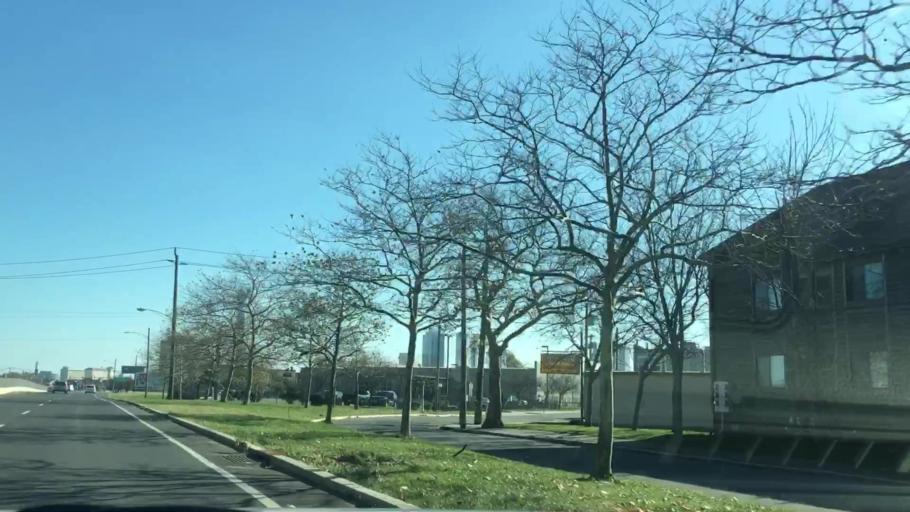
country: US
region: New Jersey
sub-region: Atlantic County
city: Atlantic City
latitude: 39.3719
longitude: -74.4348
